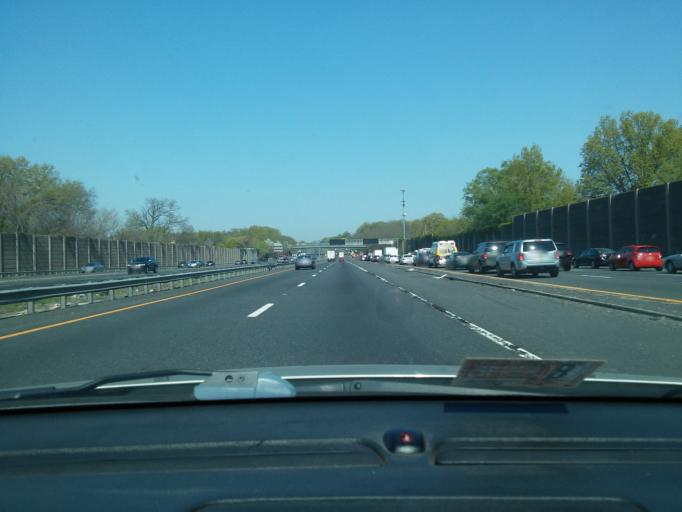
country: US
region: New Jersey
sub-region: Union County
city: Union
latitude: 40.7094
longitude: -74.2611
